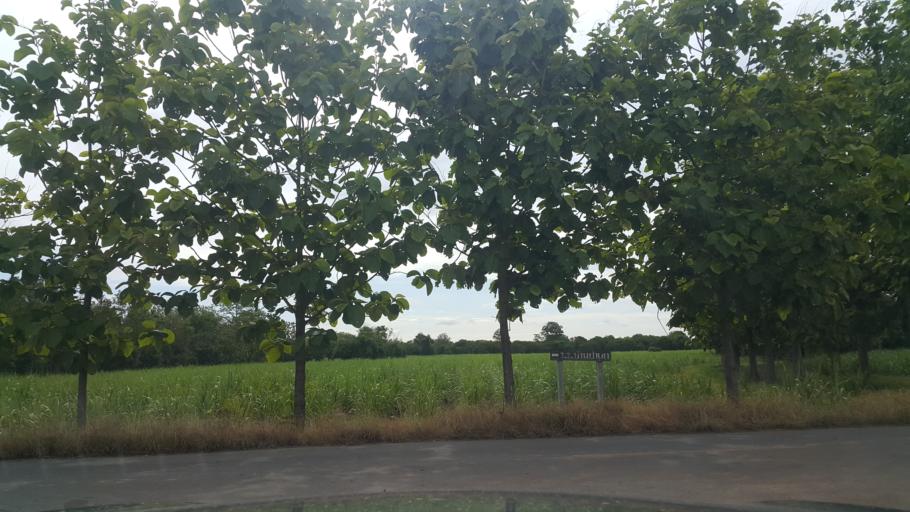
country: TH
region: Sukhothai
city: Sawankhalok
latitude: 17.2779
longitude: 99.9043
